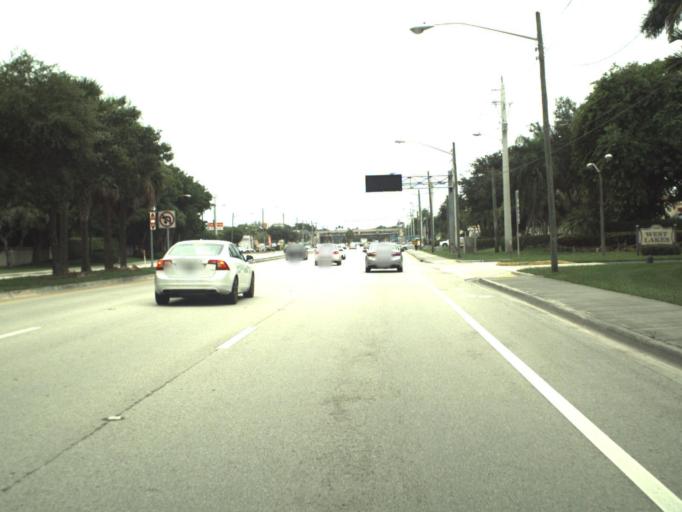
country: US
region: Florida
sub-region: Palm Beach County
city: Boca Del Mar
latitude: 26.3678
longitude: -80.1763
